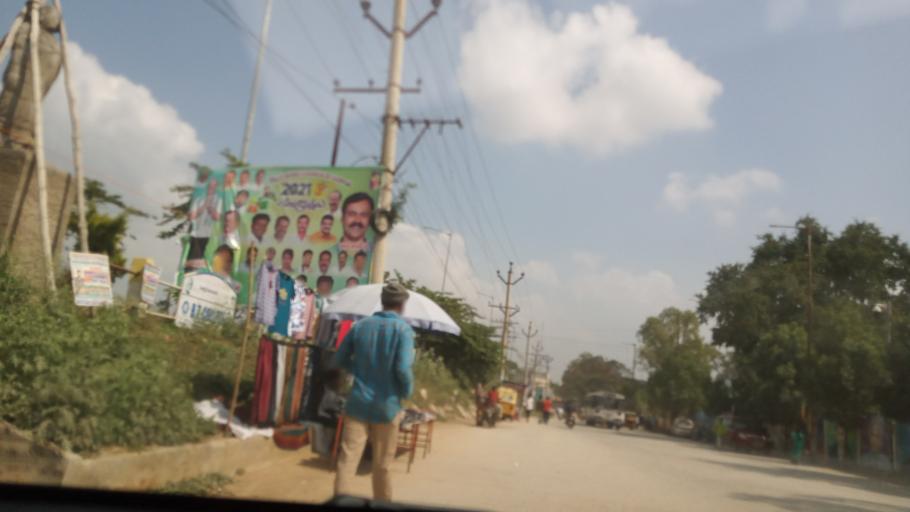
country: IN
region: Andhra Pradesh
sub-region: Chittoor
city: Madanapalle
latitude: 13.5574
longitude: 78.5047
